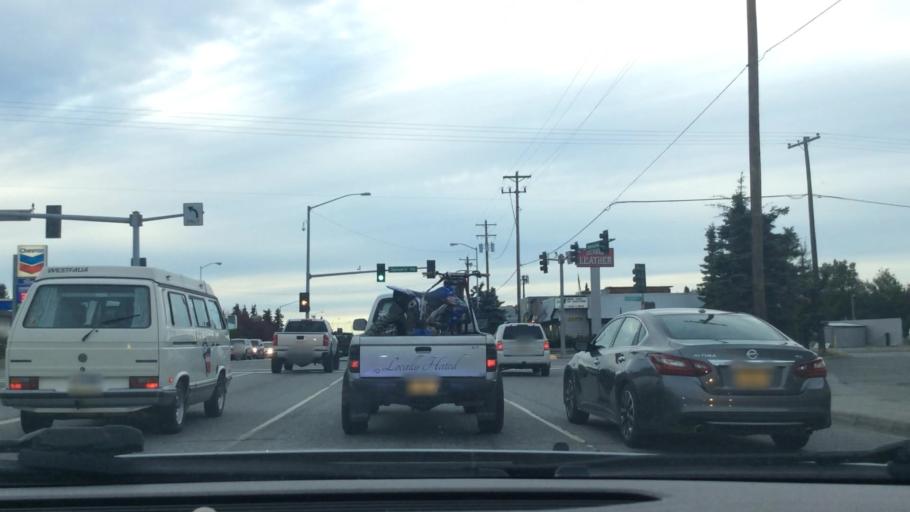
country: US
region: Alaska
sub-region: Anchorage Municipality
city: Anchorage
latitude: 61.1863
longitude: -149.9128
